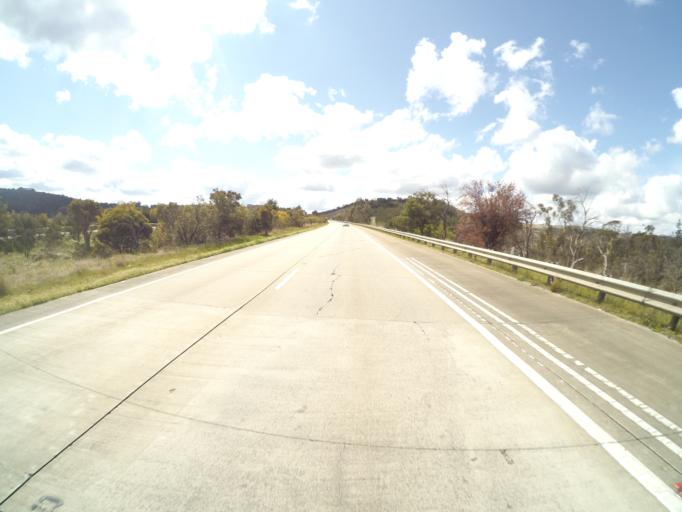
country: AU
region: New South Wales
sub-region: Wingecarribee
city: Bowral
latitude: -34.4637
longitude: 150.3528
